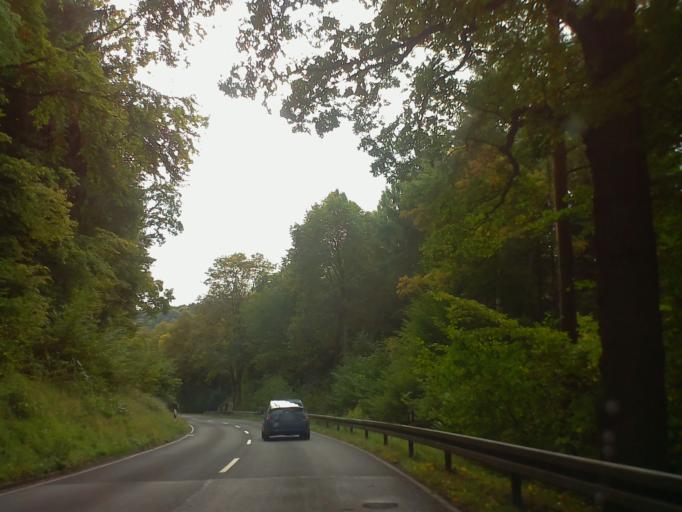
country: DE
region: Hesse
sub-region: Regierungsbezirk Kassel
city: Burghaun
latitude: 50.7164
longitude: 9.7211
